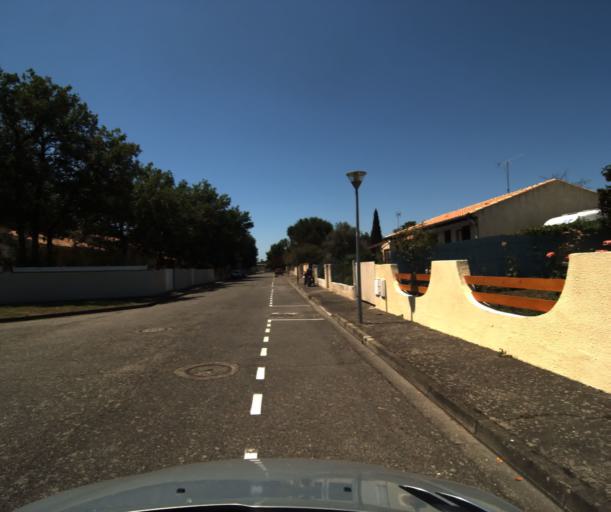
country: FR
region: Midi-Pyrenees
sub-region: Departement de la Haute-Garonne
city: Roquettes
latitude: 43.4959
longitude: 1.3765
